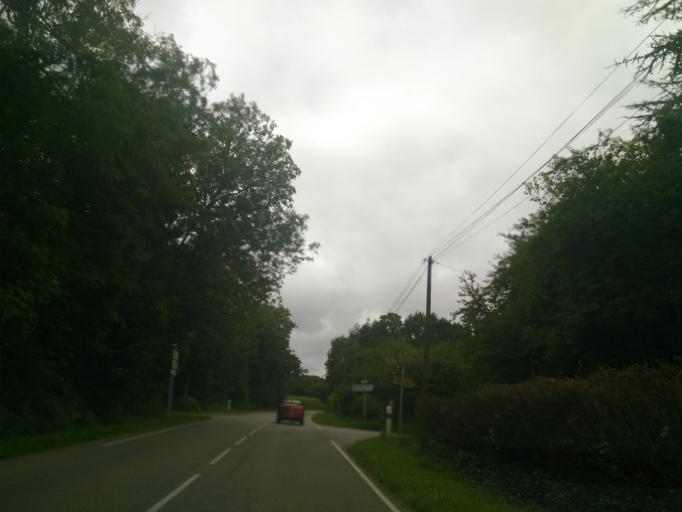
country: FR
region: Brittany
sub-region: Departement du Finistere
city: Poullan-sur-Mer
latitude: 48.0561
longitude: -4.3829
